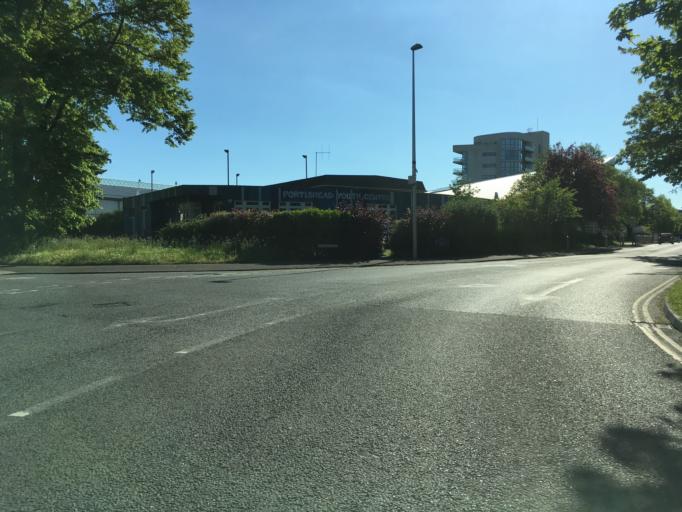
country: GB
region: England
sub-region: North Somerset
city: Portishead
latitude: 51.4868
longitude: -2.7669
